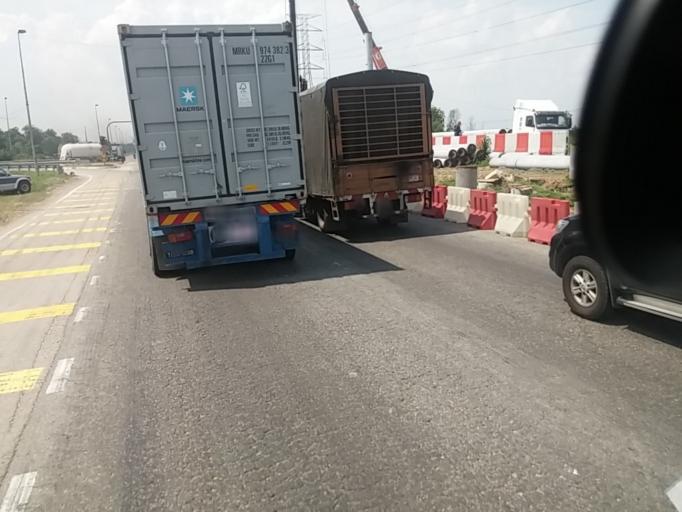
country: MY
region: Selangor
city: Klang
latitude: 2.9695
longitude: 101.3632
